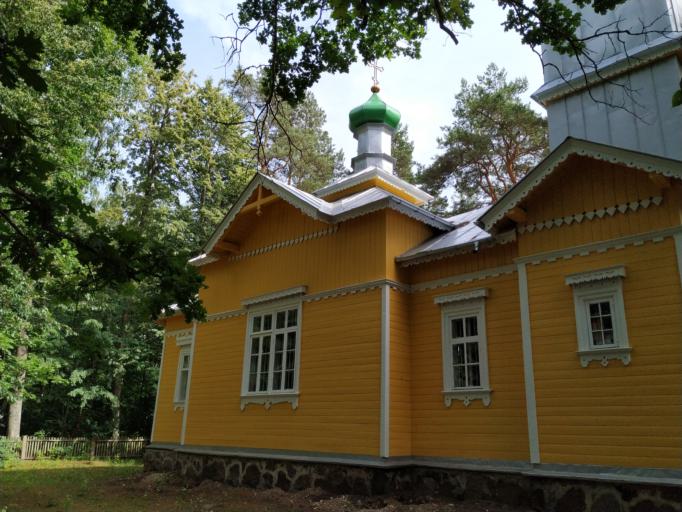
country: LT
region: Panevezys
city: Pasvalys
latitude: 55.9669
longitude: 24.3053
